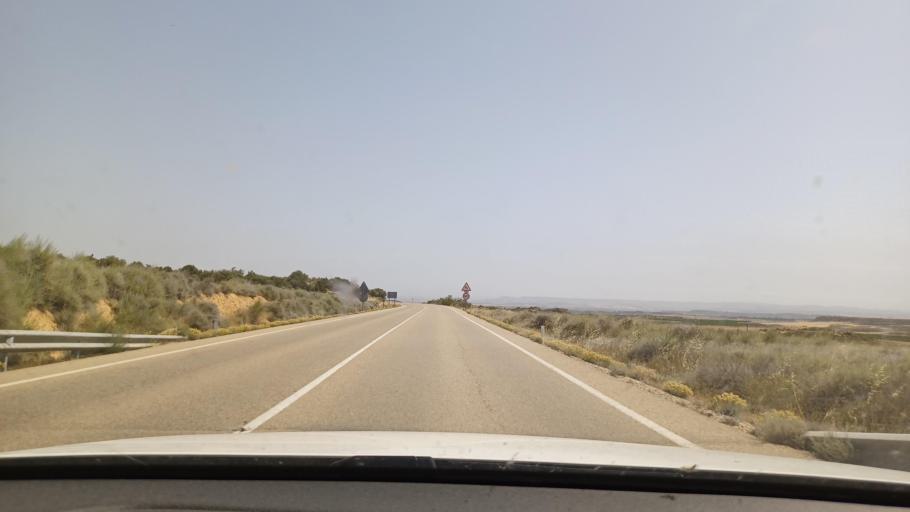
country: ES
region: Aragon
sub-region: Provincia de Zaragoza
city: Chiprana
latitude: 41.3322
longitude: -0.0893
